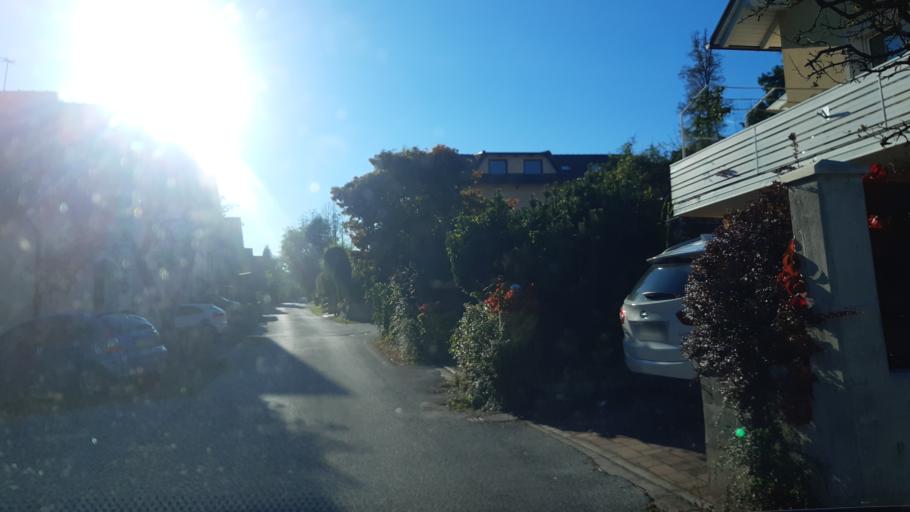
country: SI
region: Kranj
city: Kranj
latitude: 46.2357
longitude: 14.3418
